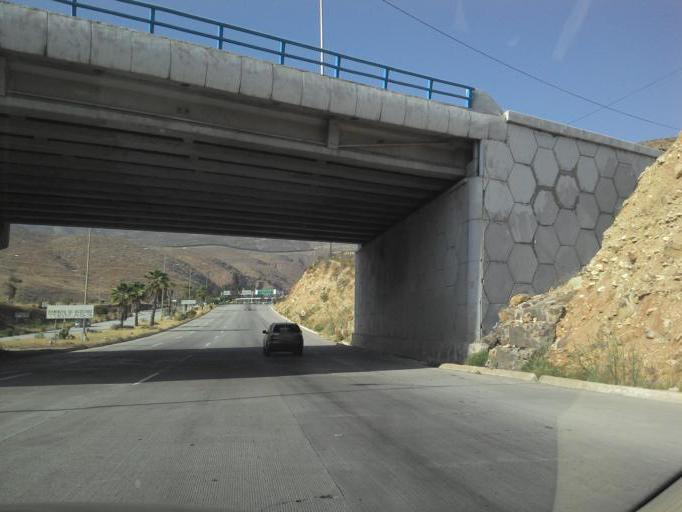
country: MX
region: Baja California
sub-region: Tijuana
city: Ejido Javier Rojo Gomez
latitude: 32.5421
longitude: -116.8544
